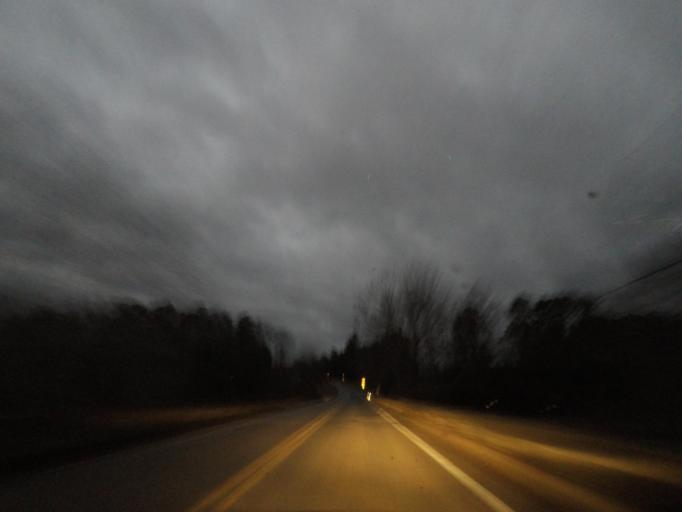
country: US
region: North Carolina
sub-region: Orange County
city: Hillsborough
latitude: 36.0467
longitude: -79.0105
